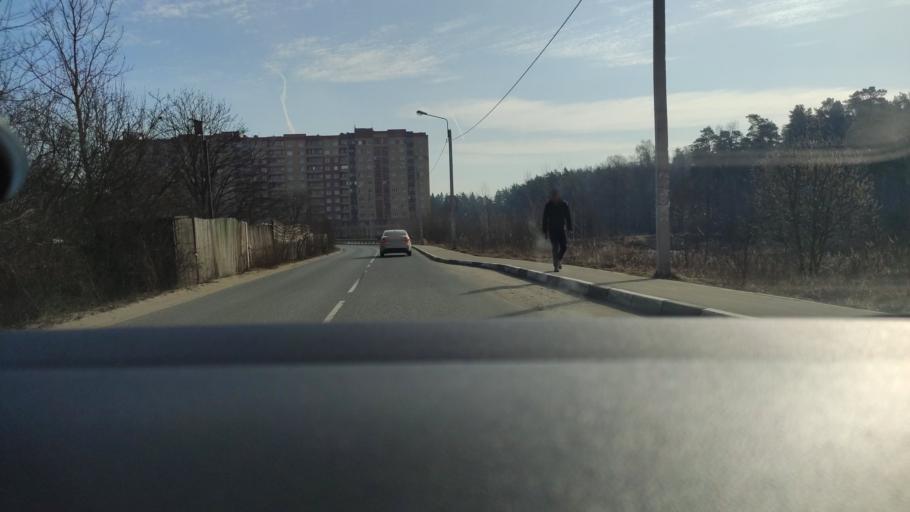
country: RU
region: Moskovskaya
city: Zarya
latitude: 55.8058
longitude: 38.0854
